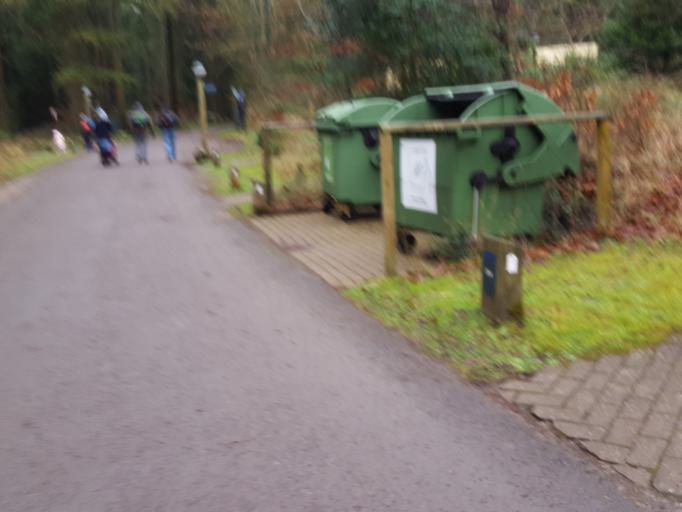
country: GB
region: England
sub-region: Wiltshire
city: Corsley
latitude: 51.1868
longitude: -2.2389
